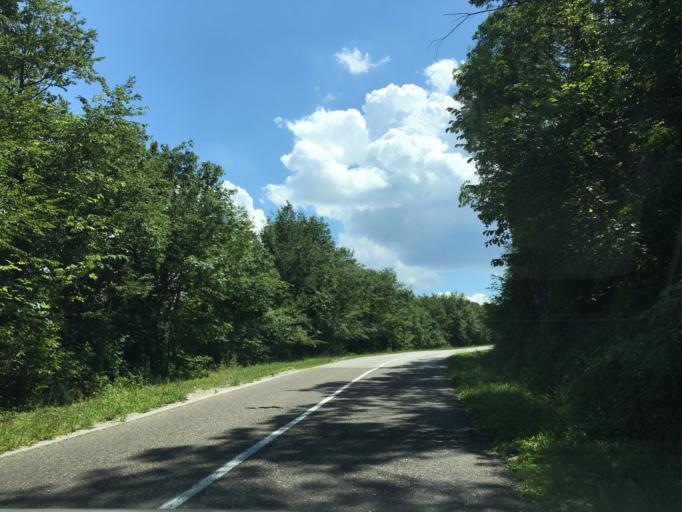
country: RS
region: Central Serbia
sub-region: Kolubarski Okrug
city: Mionica
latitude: 44.1492
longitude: 20.0207
